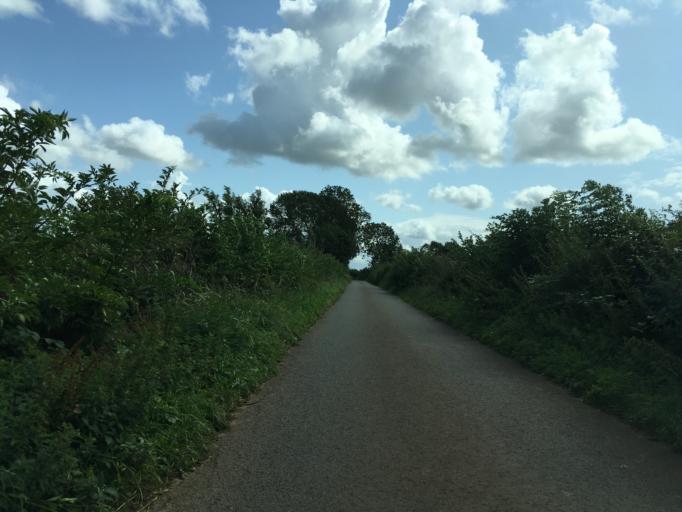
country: GB
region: England
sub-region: Wiltshire
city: Luckington
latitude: 51.6006
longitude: -2.2450
